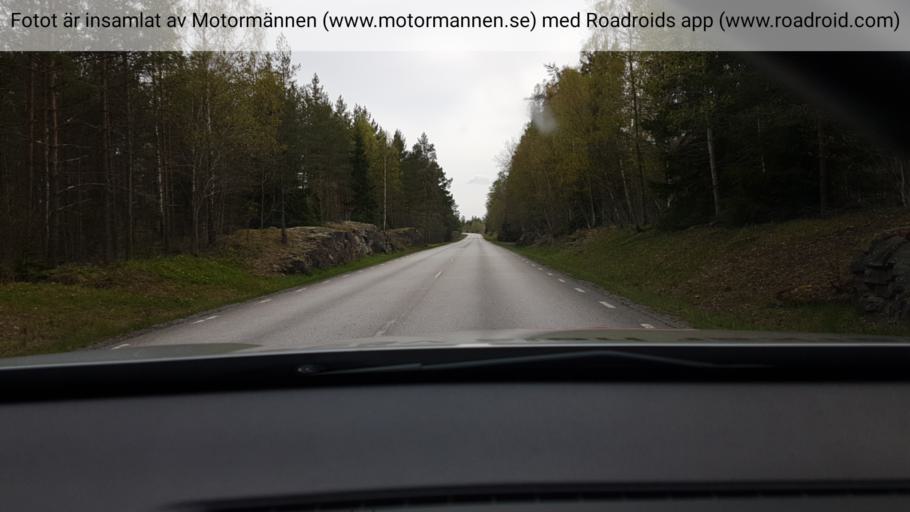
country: SE
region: Stockholm
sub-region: Norrtalje Kommun
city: Nykvarn
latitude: 59.8133
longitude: 18.0437
